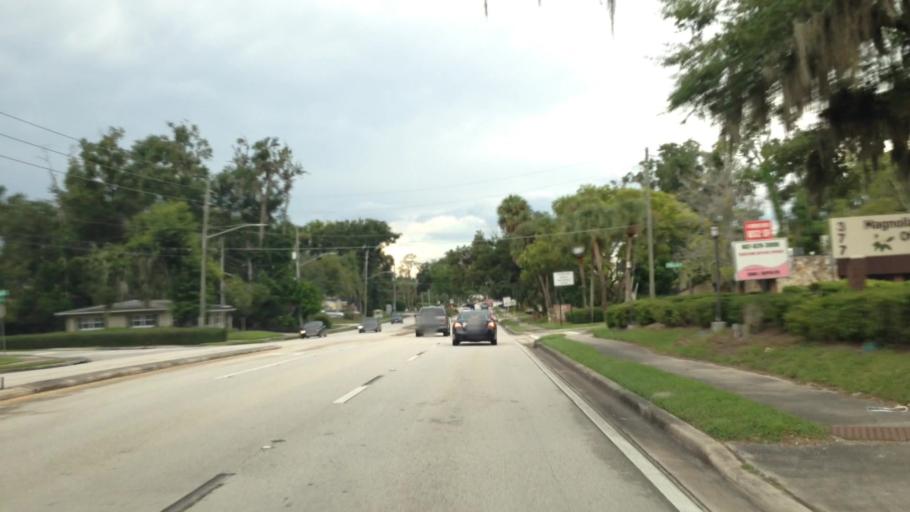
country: US
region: Florida
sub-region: Seminole County
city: Altamonte Springs
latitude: 28.6570
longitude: -81.3659
